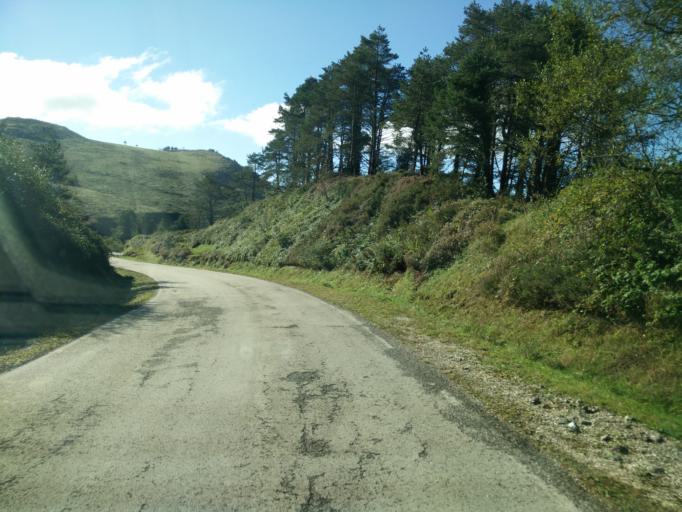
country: ES
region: Cantabria
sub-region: Provincia de Cantabria
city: San Pedro del Romeral
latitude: 43.0402
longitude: -3.8603
